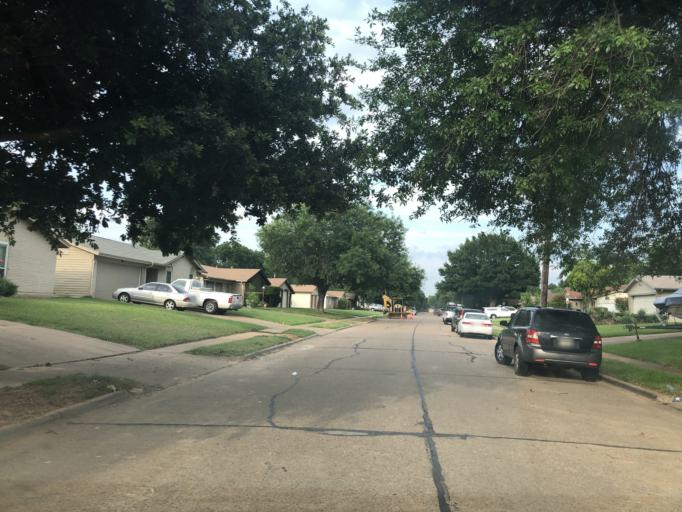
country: US
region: Texas
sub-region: Dallas County
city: Irving
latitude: 32.7875
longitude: -96.9732
